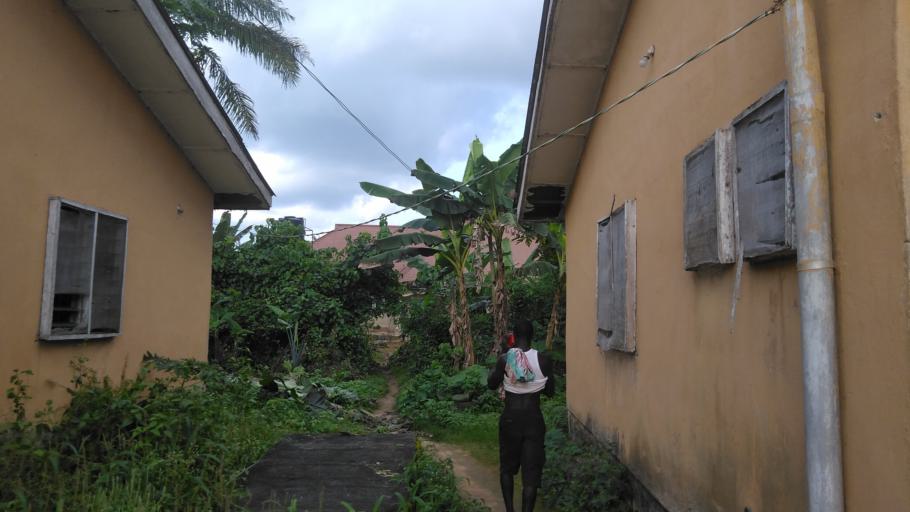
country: NG
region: Edo
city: Siluko
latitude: 6.1424
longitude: 5.2018
